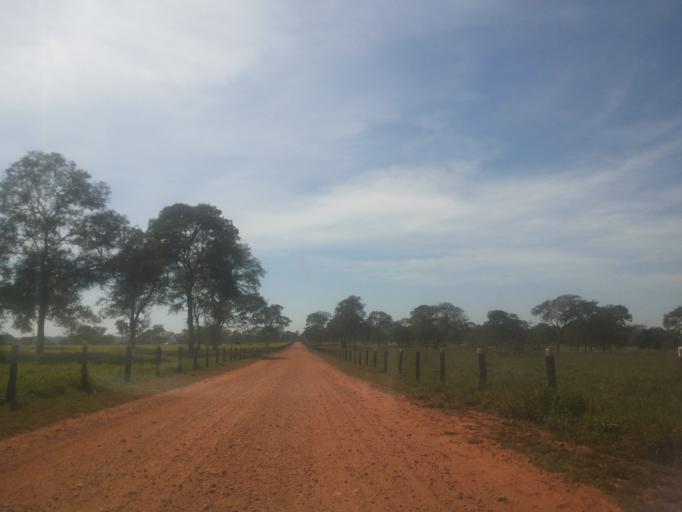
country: BR
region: Minas Gerais
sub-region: Santa Vitoria
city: Santa Vitoria
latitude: -19.0157
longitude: -50.4329
